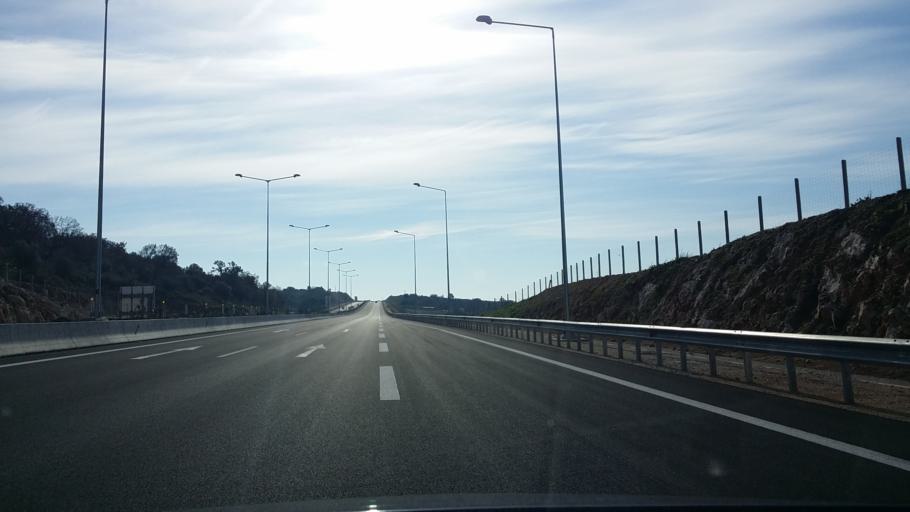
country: GR
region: West Greece
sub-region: Nomos Aitolias kai Akarnanias
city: Fitiai
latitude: 38.7449
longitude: 21.2045
